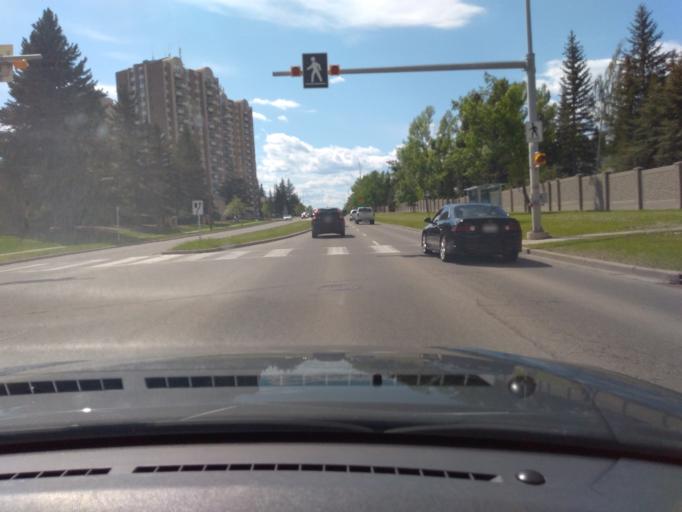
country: CA
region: Alberta
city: Calgary
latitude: 50.9723
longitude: -114.1061
